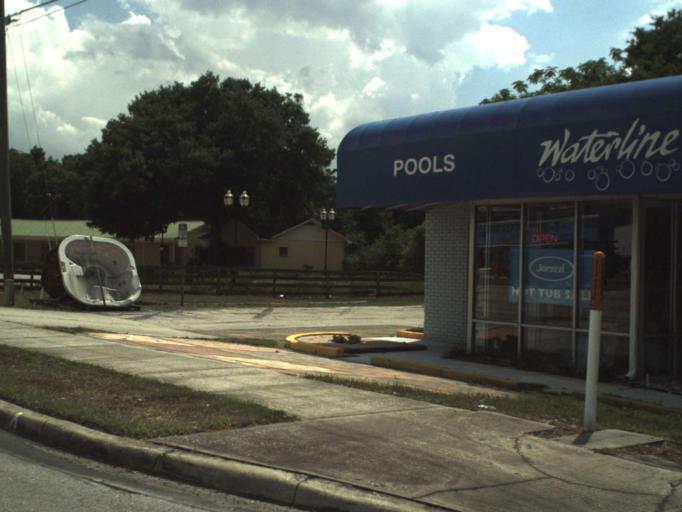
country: US
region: Florida
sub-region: Seminole County
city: Casselberry
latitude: 28.6918
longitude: -81.3280
